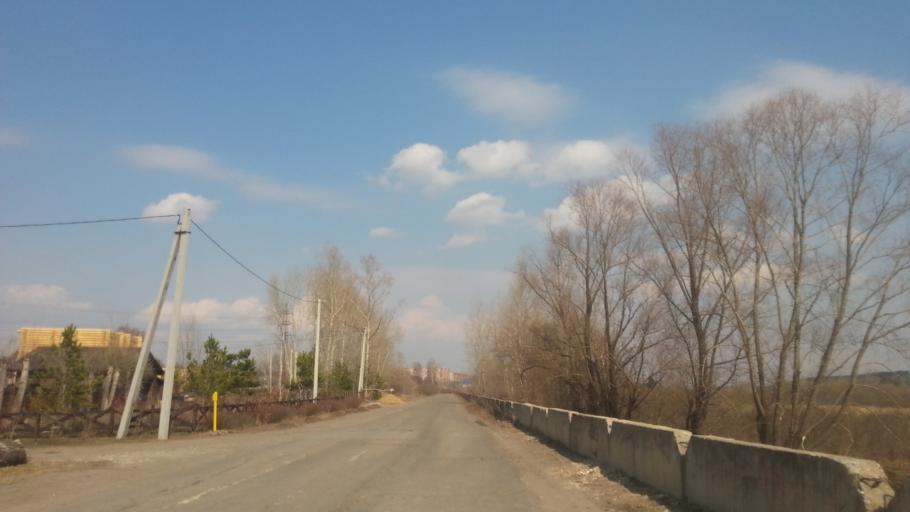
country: RU
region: Altai Krai
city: Yuzhnyy
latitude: 53.3096
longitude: 83.7222
